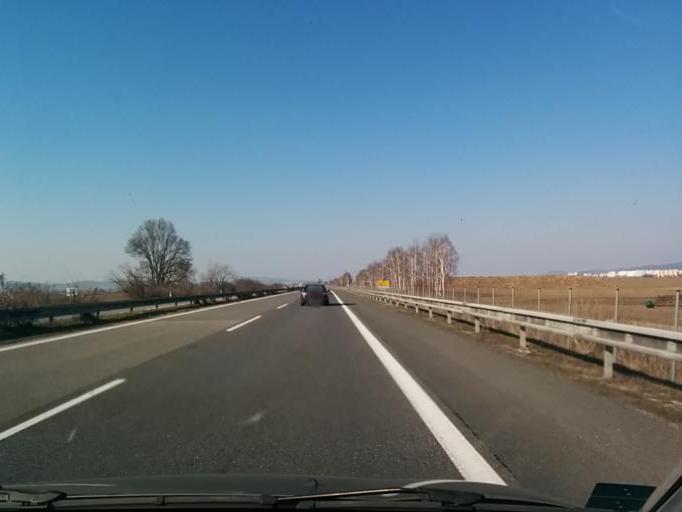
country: SK
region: Trnavsky
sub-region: Okres Trnava
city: Piestany
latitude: 48.5597
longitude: 17.7896
